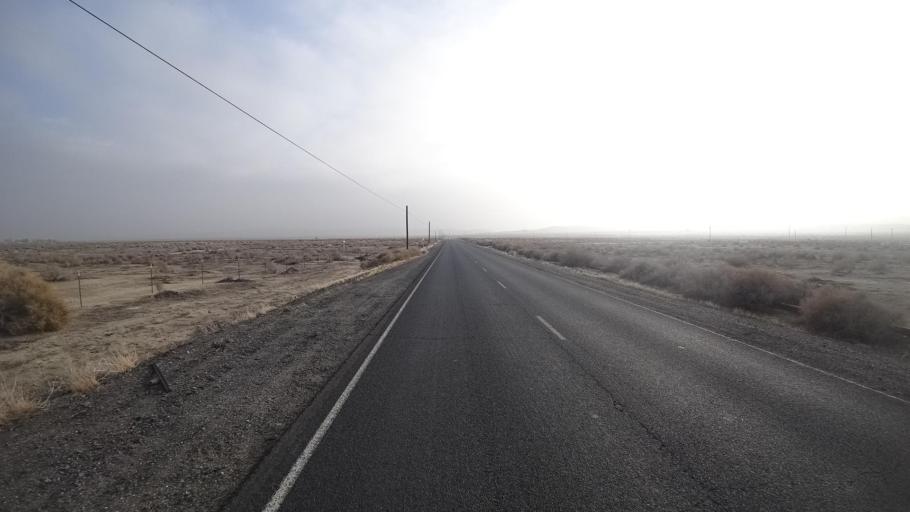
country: US
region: California
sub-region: Kern County
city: Ford City
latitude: 35.2199
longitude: -119.4456
